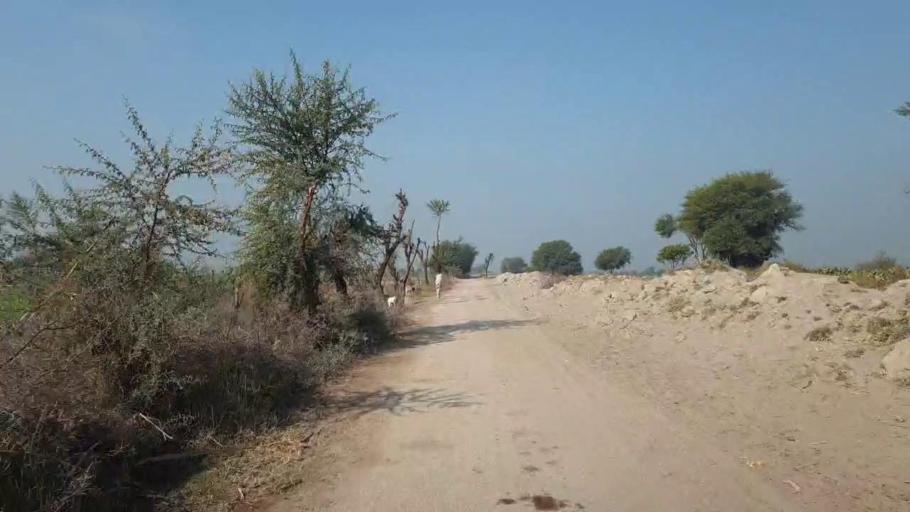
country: PK
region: Sindh
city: Shahdadpur
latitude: 26.0089
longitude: 68.5918
